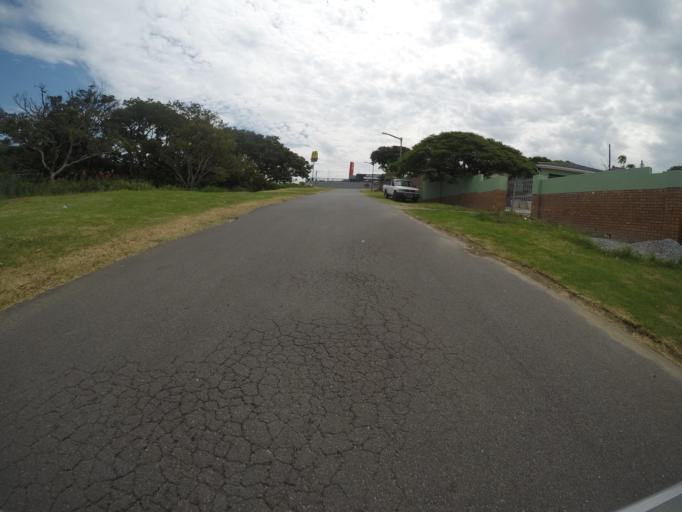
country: ZA
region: Eastern Cape
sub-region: Buffalo City Metropolitan Municipality
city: East London
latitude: -32.9939
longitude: 27.8701
